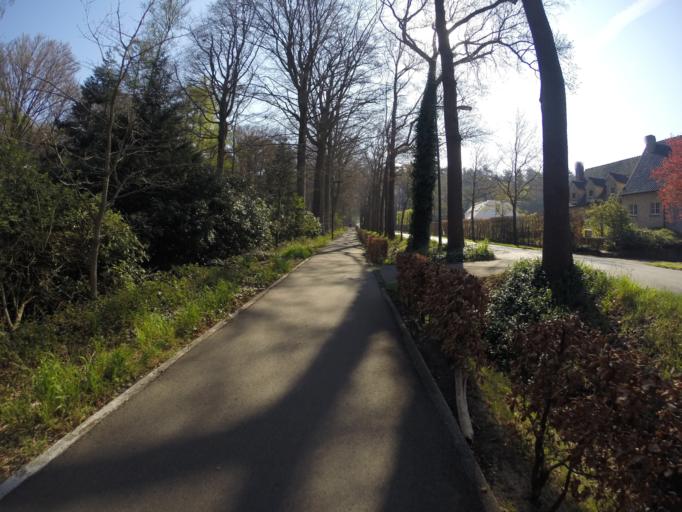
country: BE
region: Flanders
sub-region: Provincie Oost-Vlaanderen
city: Knesselare
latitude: 51.0945
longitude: 3.3828
